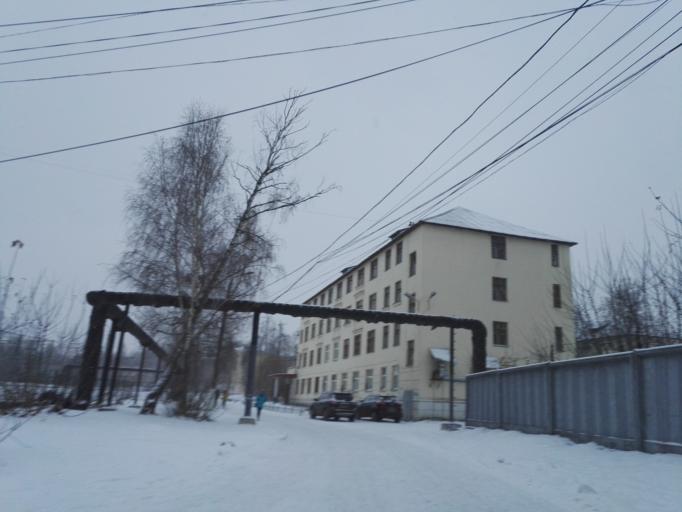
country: RU
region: Tula
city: Tula
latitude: 54.1733
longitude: 37.5906
